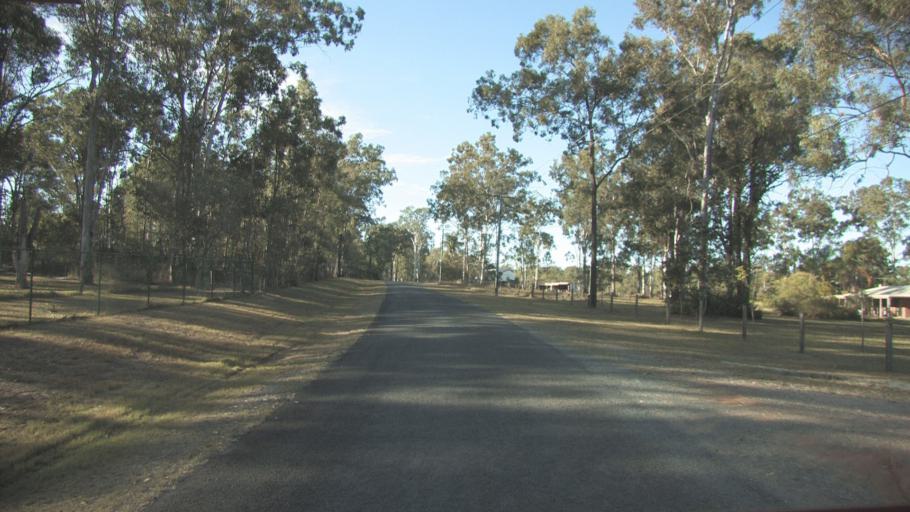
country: AU
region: Queensland
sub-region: Logan
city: Park Ridge South
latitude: -27.7247
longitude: 152.9773
